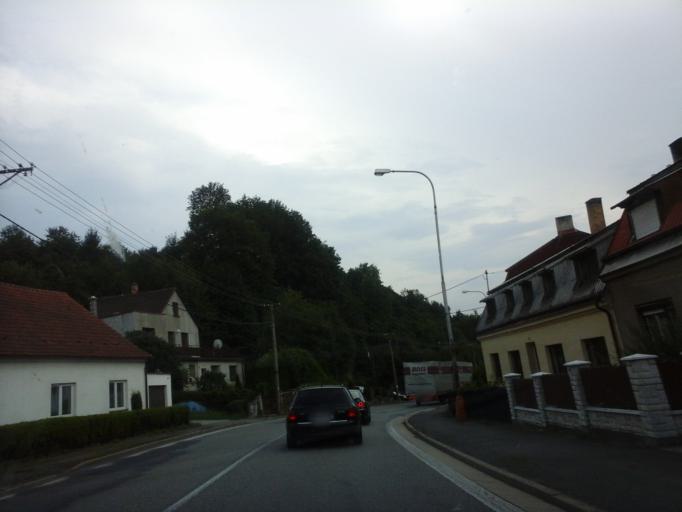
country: CZ
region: Pardubicky
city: Brnenec
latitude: 49.6183
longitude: 16.5310
